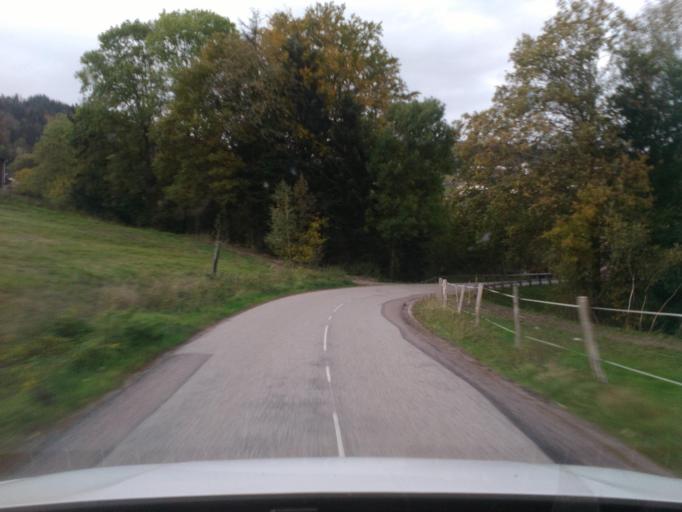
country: FR
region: Lorraine
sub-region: Departement des Vosges
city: Saint-Ame
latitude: 48.0467
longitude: 6.6788
